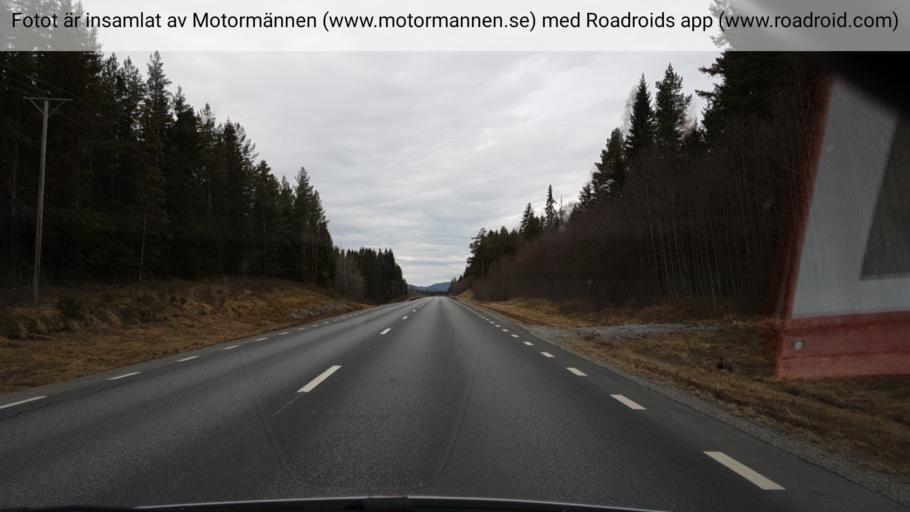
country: SE
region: Vaesternorrland
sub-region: Solleftea Kommun
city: Solleftea
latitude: 63.3561
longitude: 17.0338
